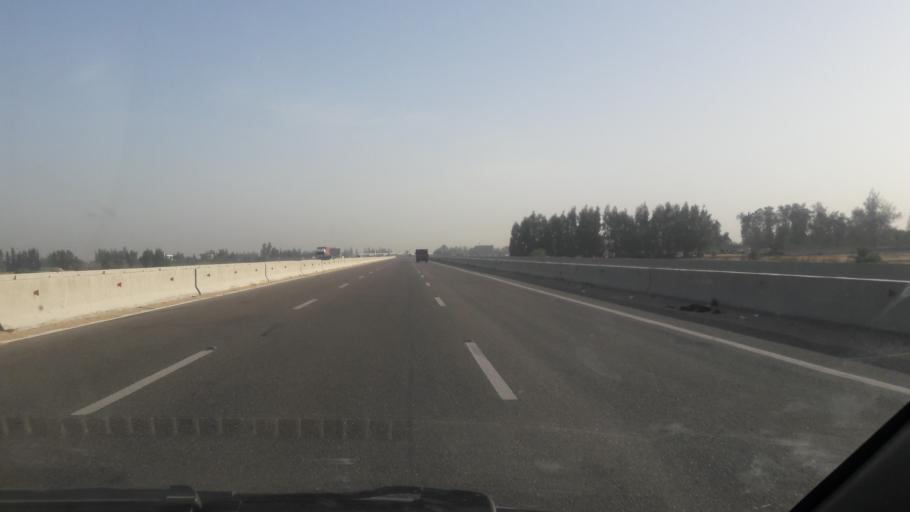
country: EG
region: Al Isma'iliyah
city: Ismailia
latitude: 30.7241
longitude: 32.1225
